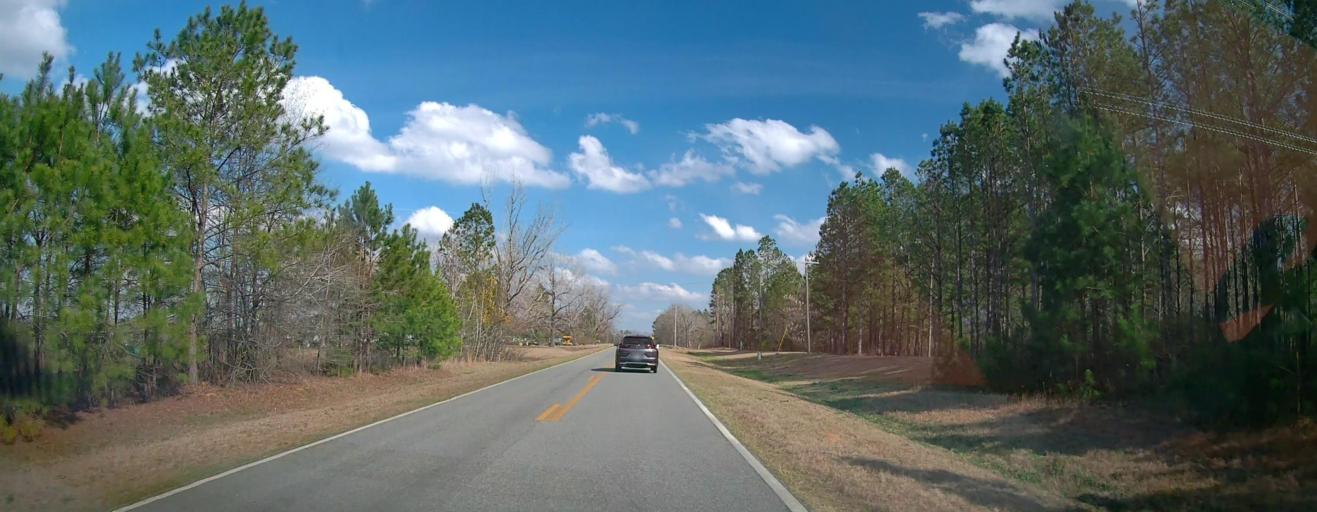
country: US
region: Georgia
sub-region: Wilkinson County
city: Irwinton
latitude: 32.6333
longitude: -83.1094
